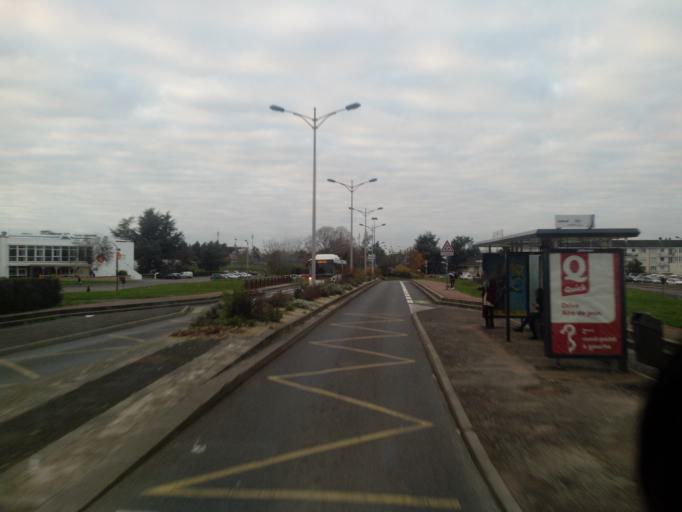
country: FR
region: Poitou-Charentes
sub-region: Departement de la Vienne
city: Saint-Benoit
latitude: 46.5700
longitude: 0.3795
